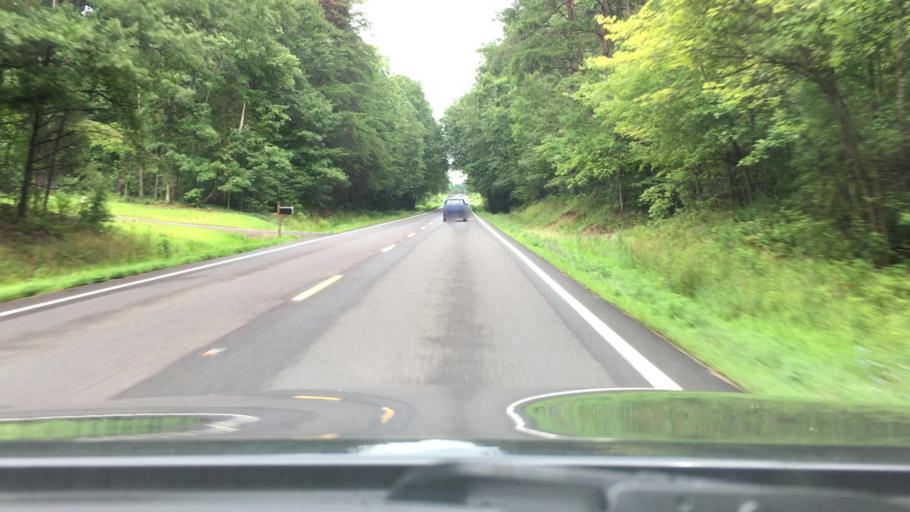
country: US
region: Virginia
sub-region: Orange County
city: Orange
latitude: 38.2695
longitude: -77.9260
